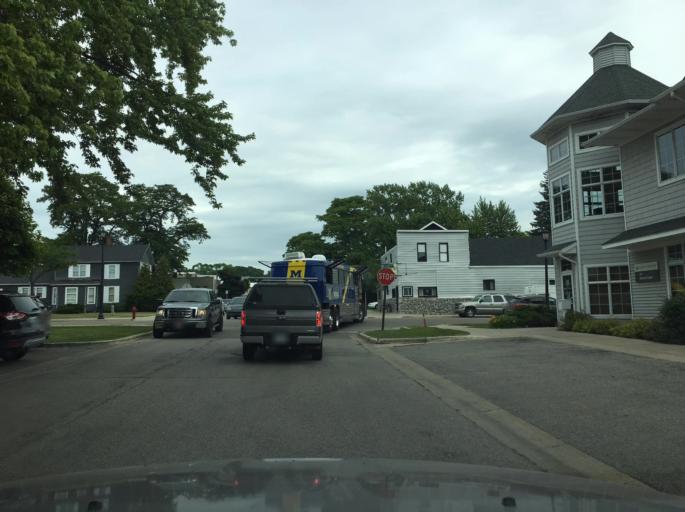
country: US
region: Michigan
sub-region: Mason County
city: Ludington
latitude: 43.9535
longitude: -86.4497
